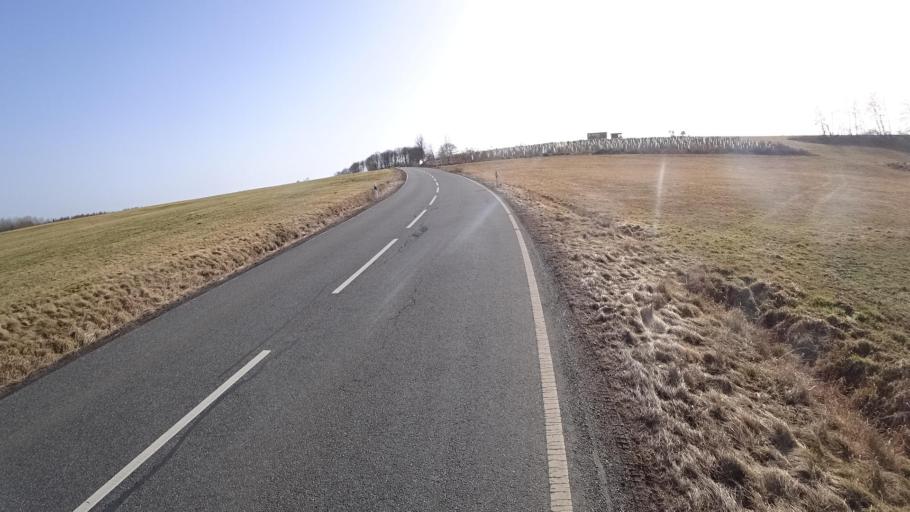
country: DE
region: Rheinland-Pfalz
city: Etzbach
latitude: 50.7758
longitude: 7.6953
